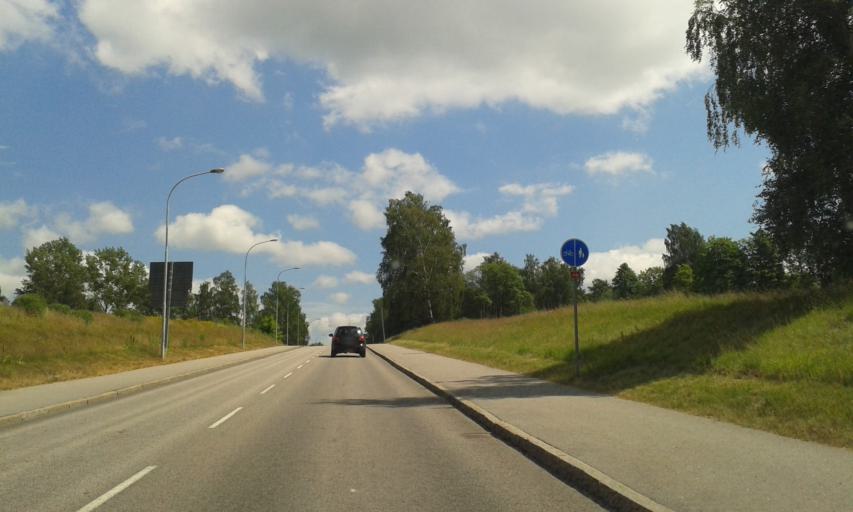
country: SE
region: Kronoberg
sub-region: Vaxjo Kommun
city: Vaexjoe
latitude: 56.8809
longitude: 14.8161
